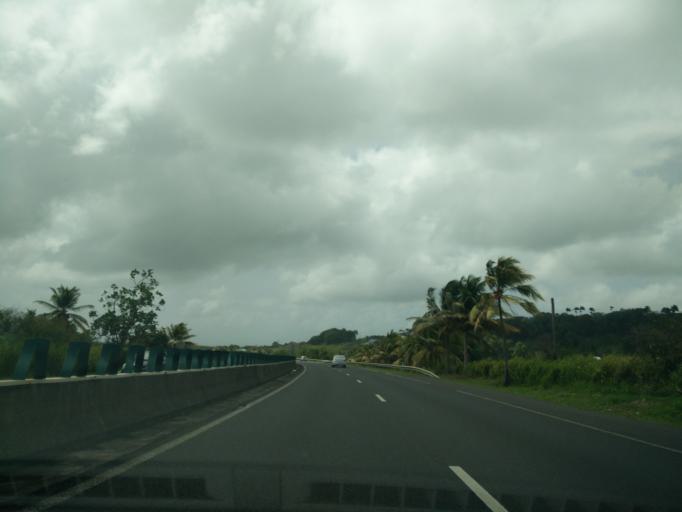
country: GP
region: Guadeloupe
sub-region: Guadeloupe
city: Petit-Bourg
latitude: 16.1841
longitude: -61.6056
